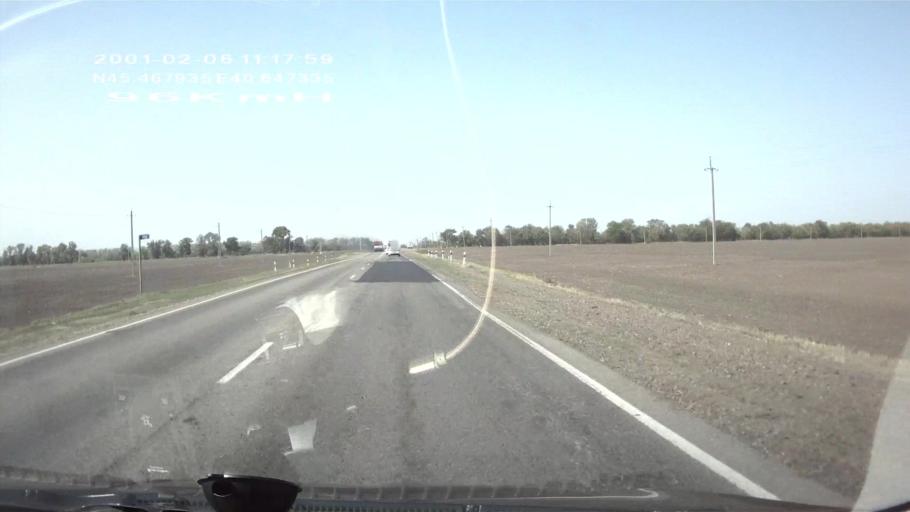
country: RU
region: Krasnodarskiy
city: Kavkazskaya
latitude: 45.4681
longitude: 40.6447
